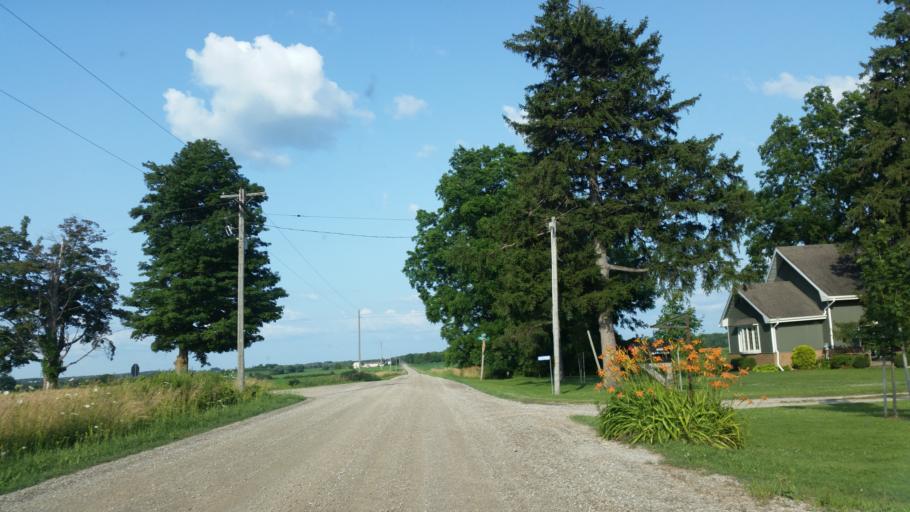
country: CA
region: Ontario
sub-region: Oxford County
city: Woodstock
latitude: 43.0499
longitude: -80.5941
